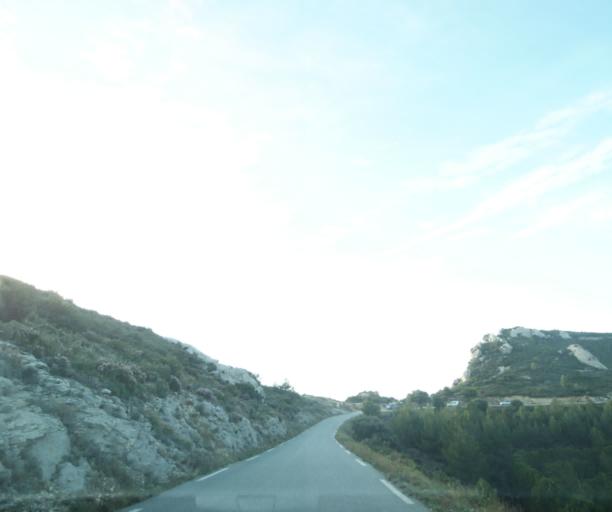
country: FR
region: Provence-Alpes-Cote d'Azur
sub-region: Departement des Bouches-du-Rhone
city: Cassis
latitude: 43.1859
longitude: 5.5630
